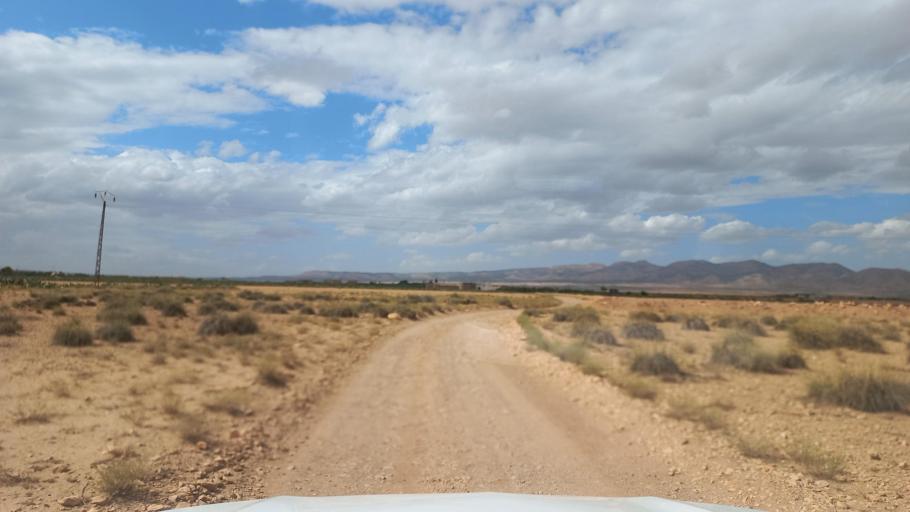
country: TN
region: Al Qasrayn
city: Sbiba
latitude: 35.3817
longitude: 9.0991
